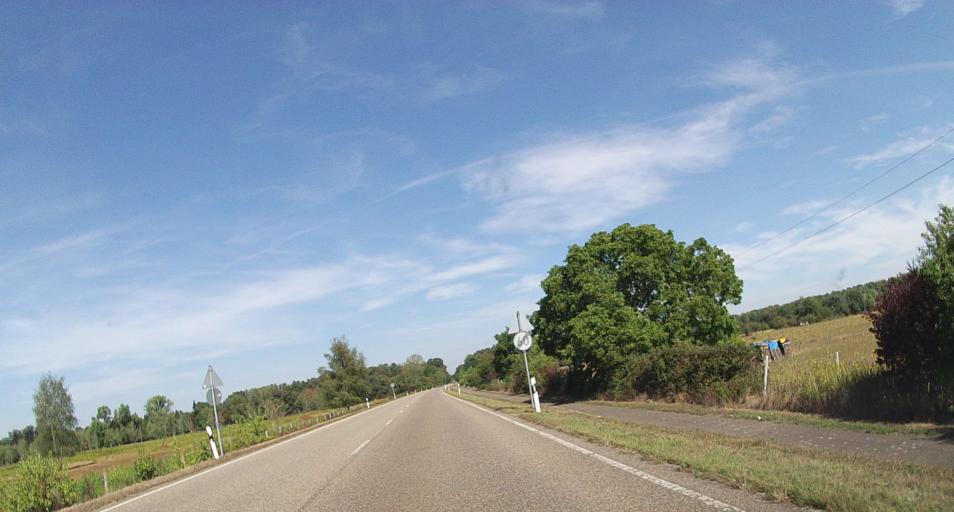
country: DE
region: Baden-Wuerttemberg
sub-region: Karlsruhe Region
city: Rastatt
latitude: 48.8202
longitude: 8.1961
